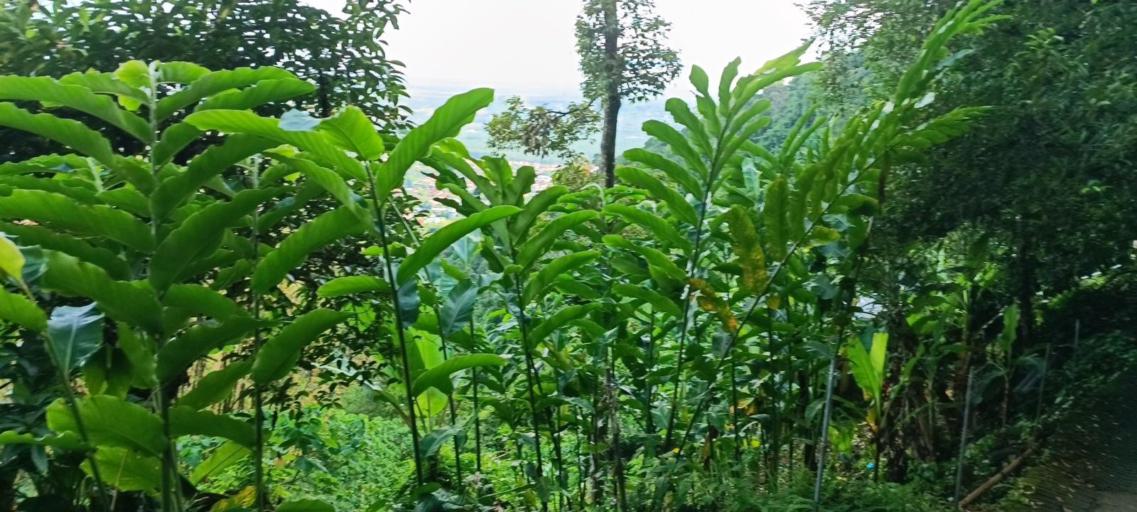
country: MY
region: Penang
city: Bukit Mertajam
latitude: 5.3703
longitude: 100.4806
